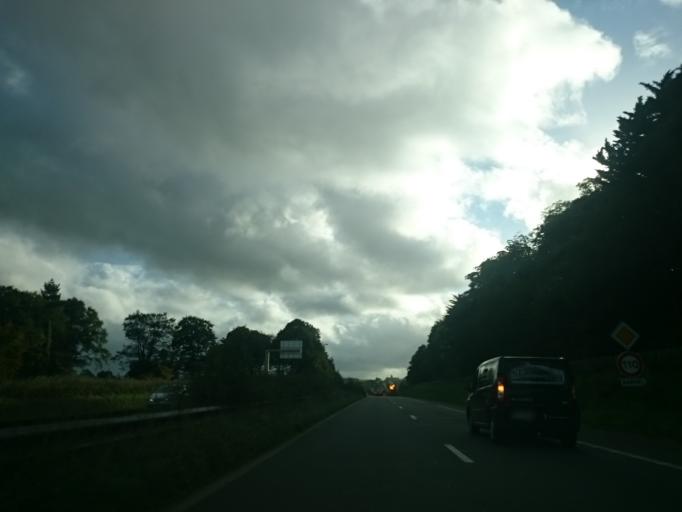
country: FR
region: Brittany
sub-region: Departement du Finistere
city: Morlaix
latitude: 48.5663
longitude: -3.8580
